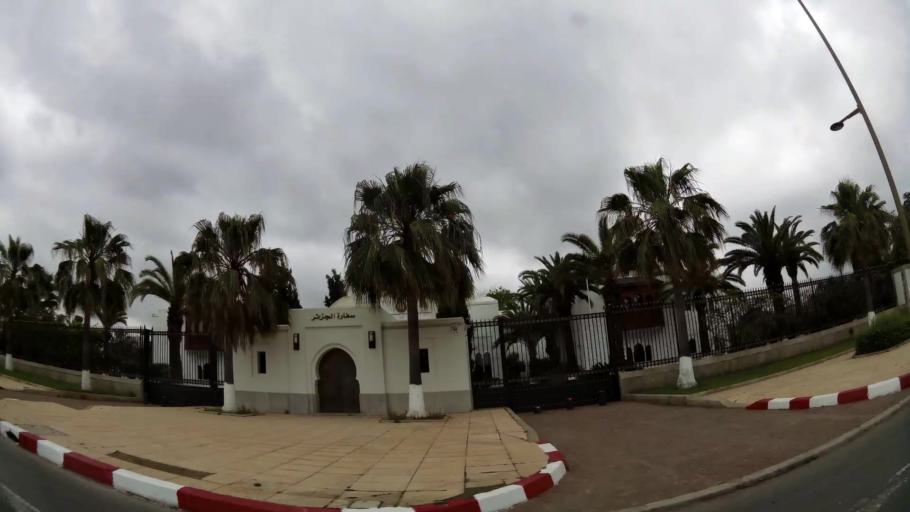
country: MA
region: Rabat-Sale-Zemmour-Zaer
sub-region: Rabat
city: Rabat
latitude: 33.9674
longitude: -6.8281
